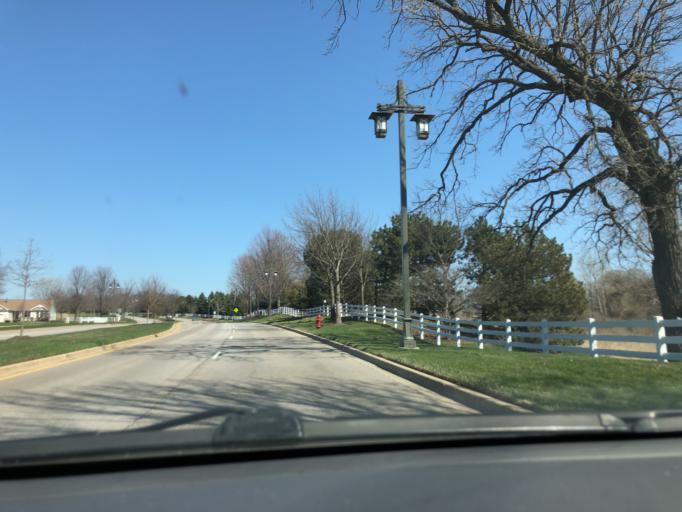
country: US
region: Illinois
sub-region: McHenry County
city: Huntley
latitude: 42.1365
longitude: -88.4435
